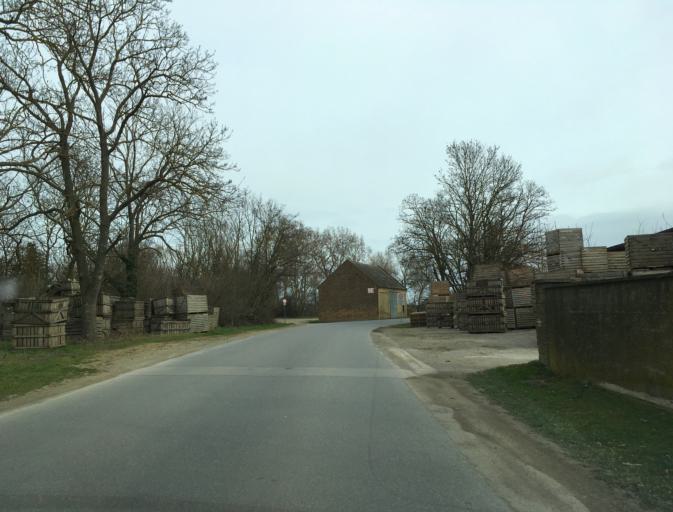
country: AT
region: Lower Austria
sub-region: Politischer Bezirk Ganserndorf
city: Glinzendorf
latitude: 48.2488
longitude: 16.6407
